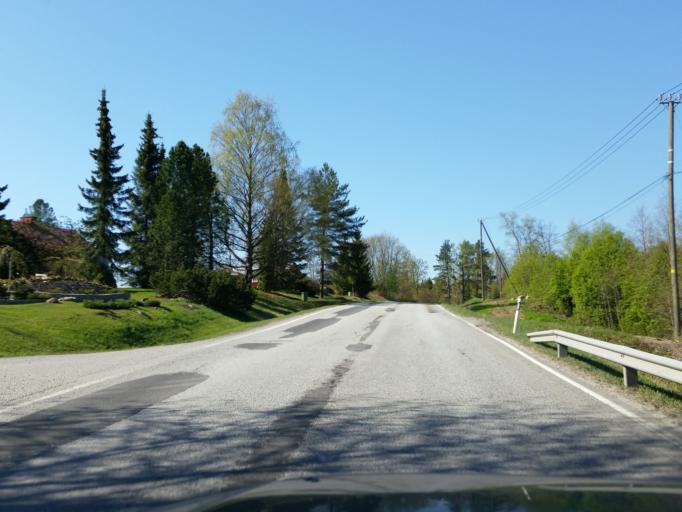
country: FI
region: Uusimaa
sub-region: Helsinki
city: Lohja
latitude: 60.1793
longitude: 24.0084
